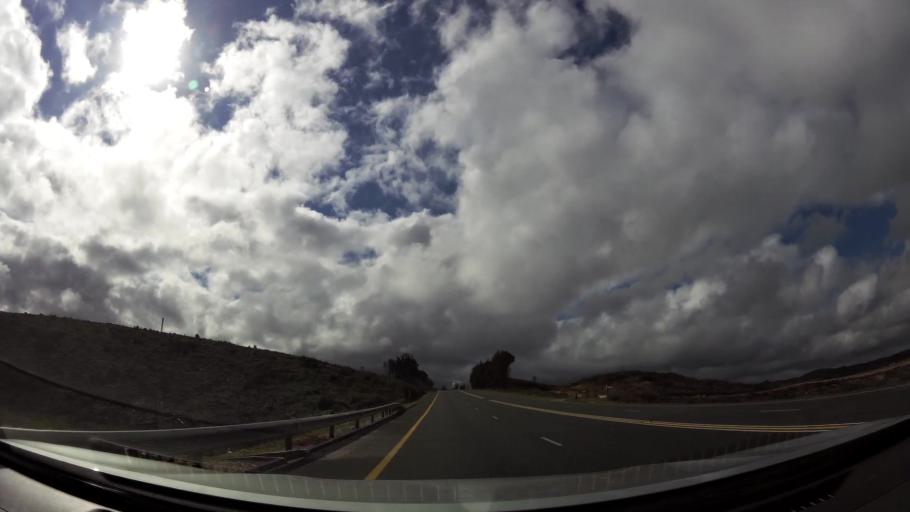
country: ZA
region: Western Cape
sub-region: Eden District Municipality
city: Knysna
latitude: -34.0395
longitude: 23.1202
